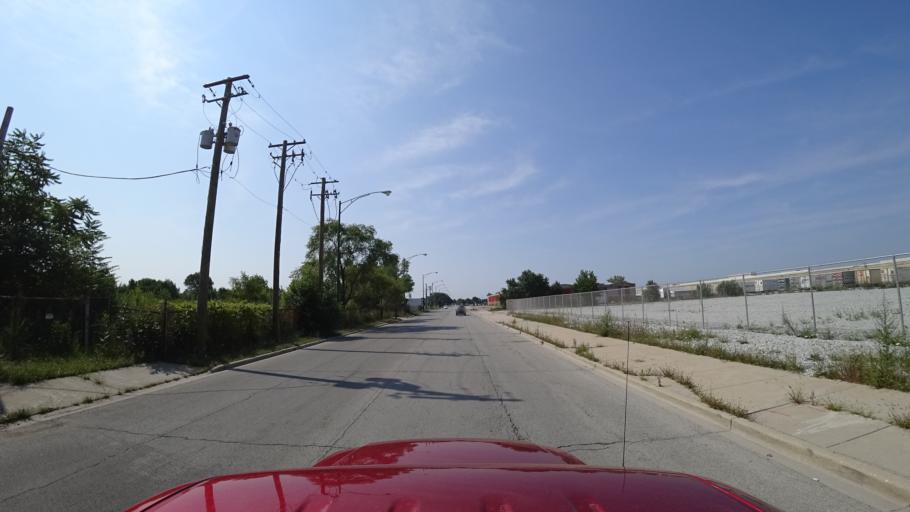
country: US
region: Illinois
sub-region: Cook County
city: Hometown
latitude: 41.7615
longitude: -87.7326
